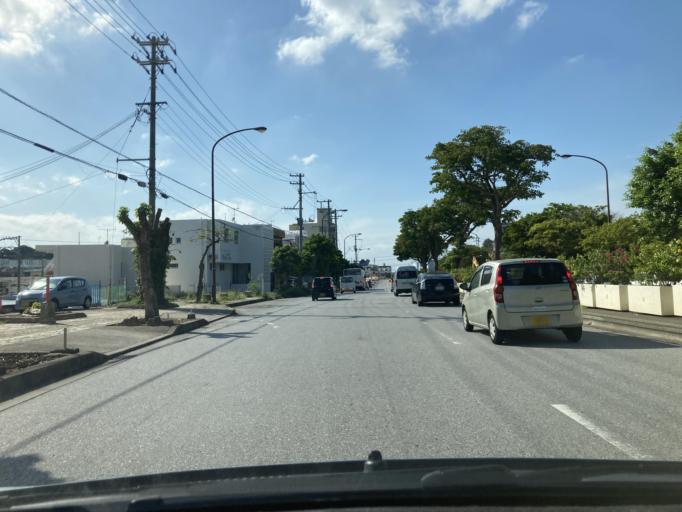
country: JP
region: Okinawa
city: Chatan
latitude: 26.2961
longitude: 127.7822
